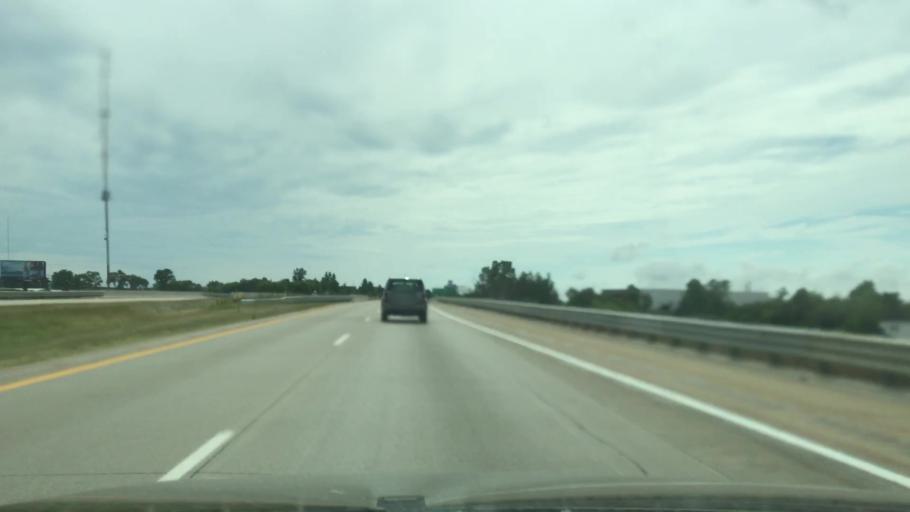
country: US
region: Michigan
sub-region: Kent County
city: Walker
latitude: 43.0189
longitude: -85.7356
